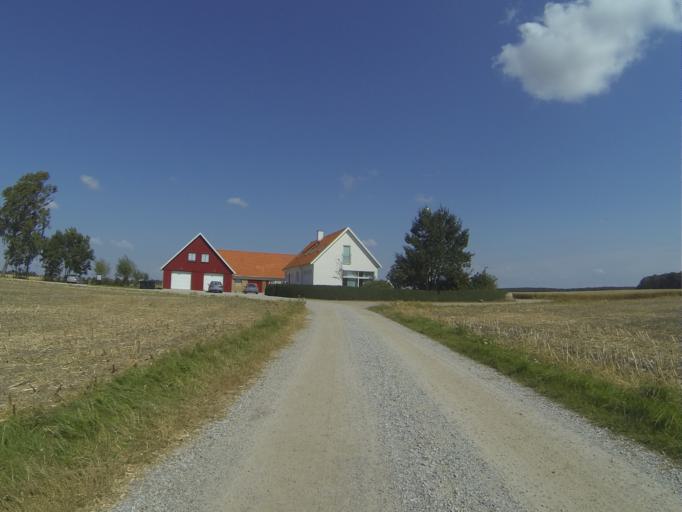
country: SE
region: Skane
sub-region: Lunds Kommun
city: Lund
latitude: 55.7266
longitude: 13.2682
